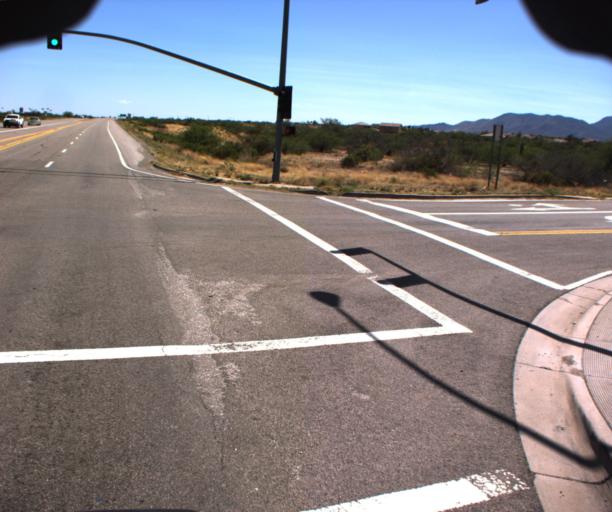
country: US
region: Arizona
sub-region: Cochise County
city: Whetstone
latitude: 31.9618
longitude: -110.3455
